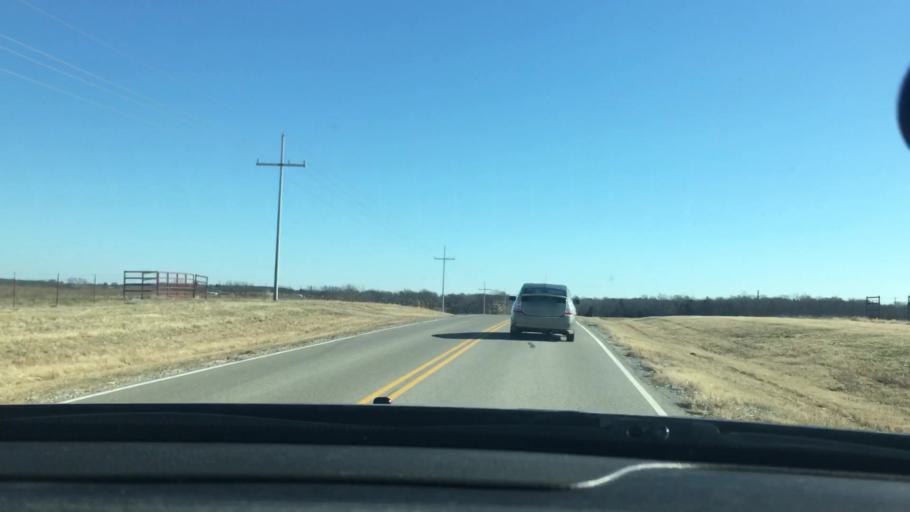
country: US
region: Oklahoma
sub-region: Murray County
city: Davis
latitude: 34.4772
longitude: -97.0781
